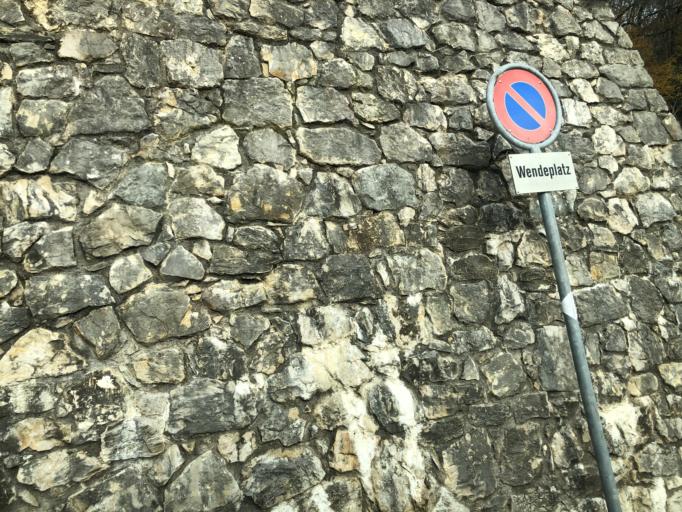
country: CH
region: Aargau
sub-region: Bezirk Baden
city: Wettingen
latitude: 47.4742
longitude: 8.3145
